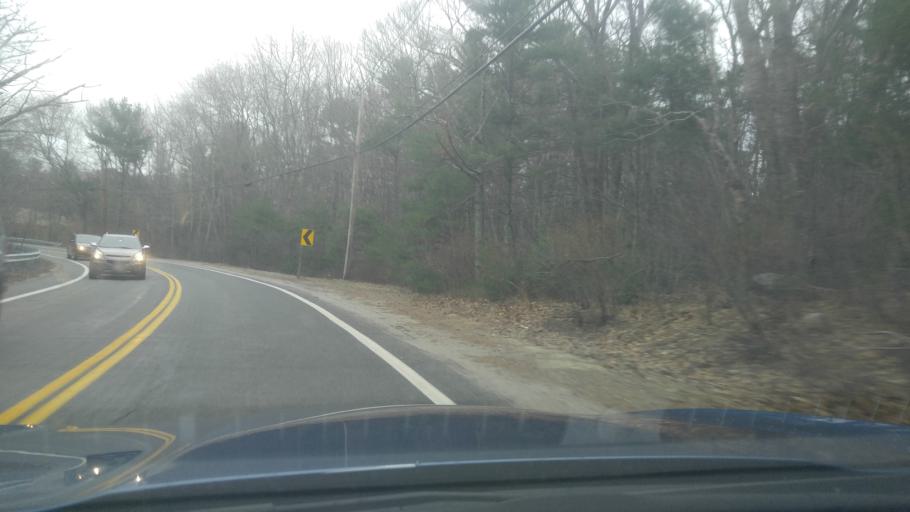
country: US
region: Rhode Island
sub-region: Kent County
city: West Greenwich
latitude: 41.6649
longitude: -71.6175
